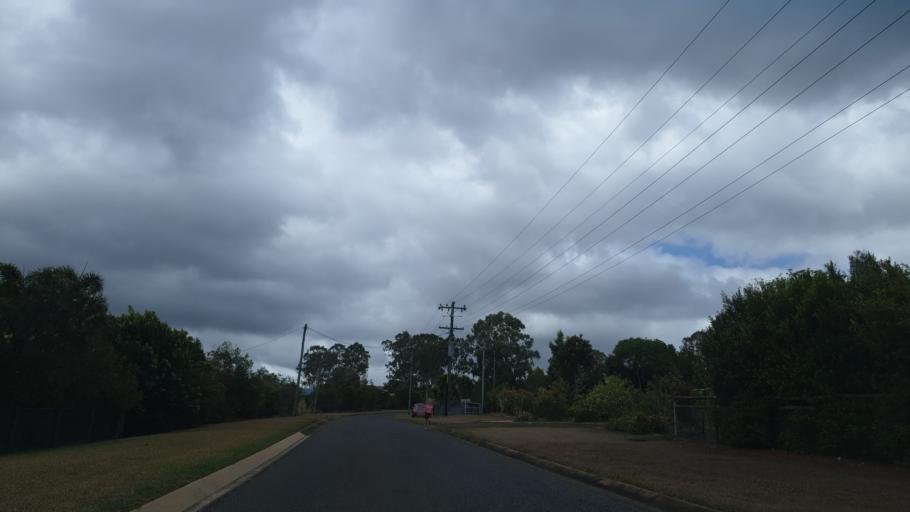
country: AU
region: Queensland
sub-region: Tablelands
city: Tolga
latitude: -17.2105
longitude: 145.4419
